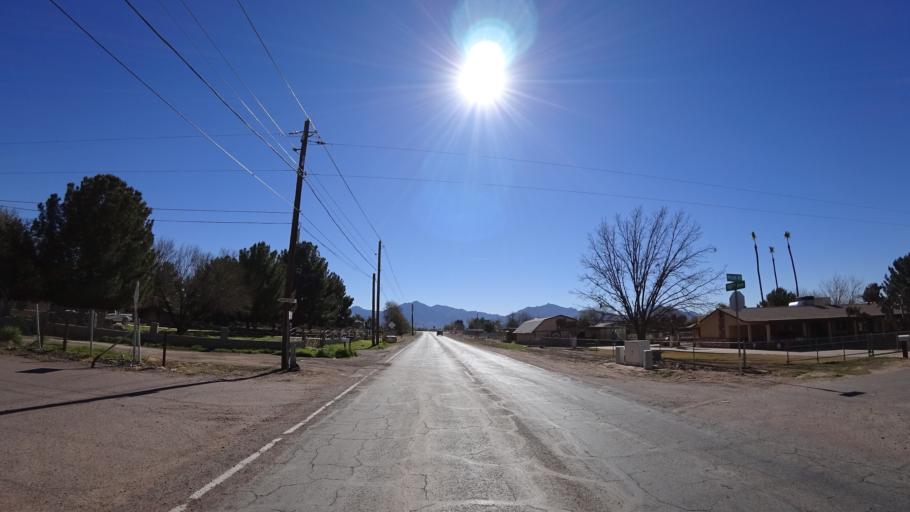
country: US
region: Arizona
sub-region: Maricopa County
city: Tolleson
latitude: 33.3947
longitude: -112.2891
